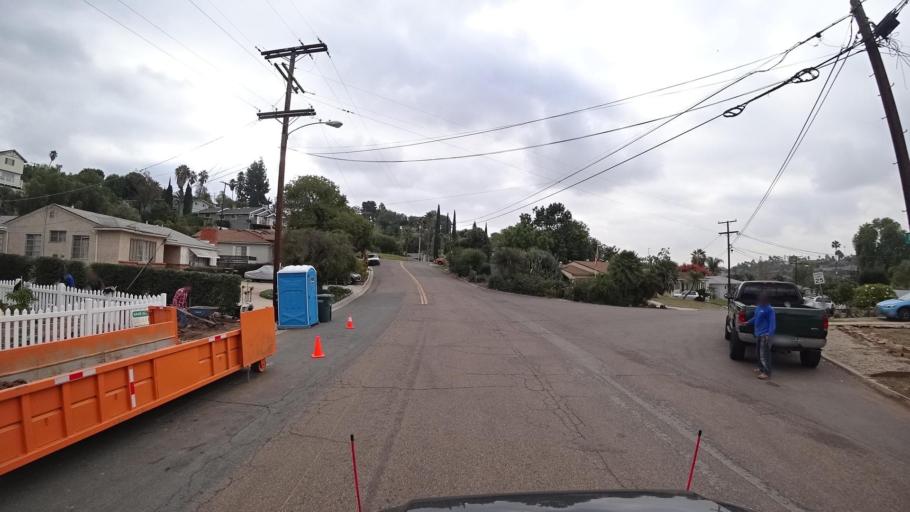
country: US
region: California
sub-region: San Diego County
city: Spring Valley
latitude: 32.7478
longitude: -117.0121
